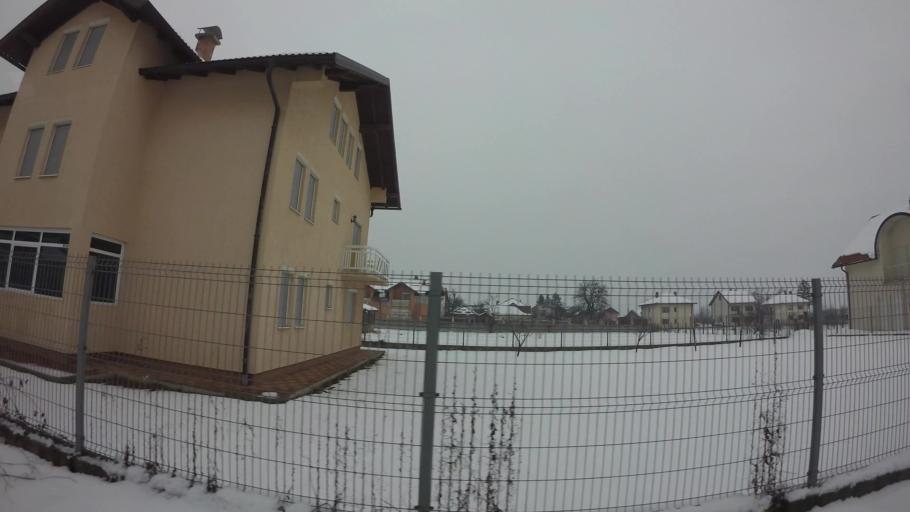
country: BA
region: Federation of Bosnia and Herzegovina
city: Hadzici
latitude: 43.8462
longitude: 18.2792
